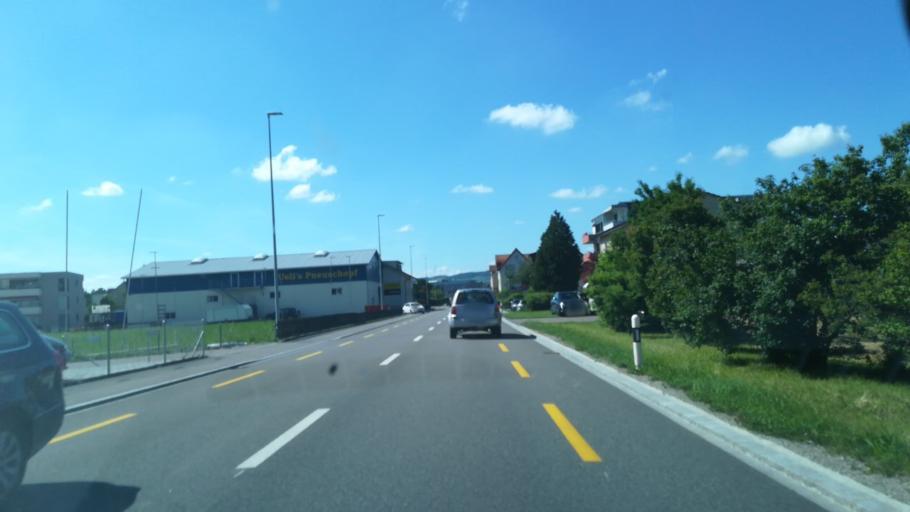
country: CH
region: Thurgau
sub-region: Weinfelden District
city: Sulgen
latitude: 47.5317
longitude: 9.1897
